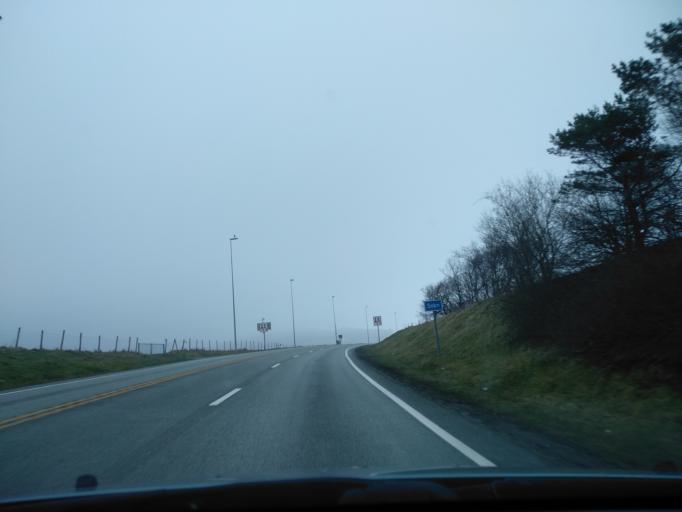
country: NO
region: Rogaland
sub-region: Rennesoy
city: Vikevag
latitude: 59.0553
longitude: 5.6575
